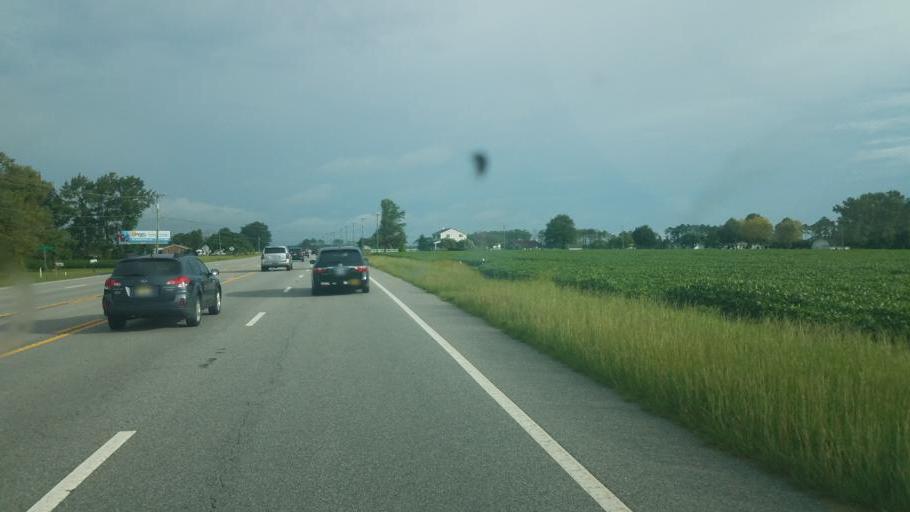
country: US
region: North Carolina
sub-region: Currituck County
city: Currituck
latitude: 36.3925
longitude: -75.9803
